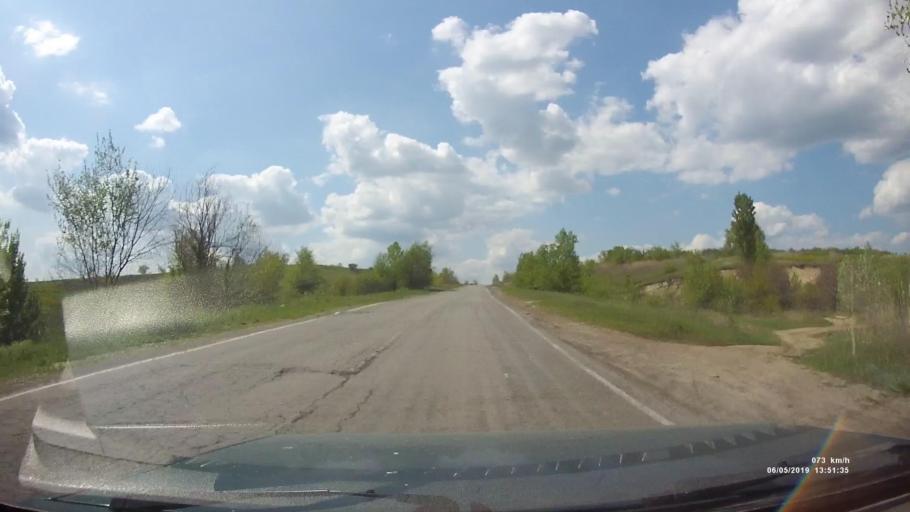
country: RU
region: Rostov
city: Melikhovskaya
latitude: 47.6576
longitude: 40.4897
